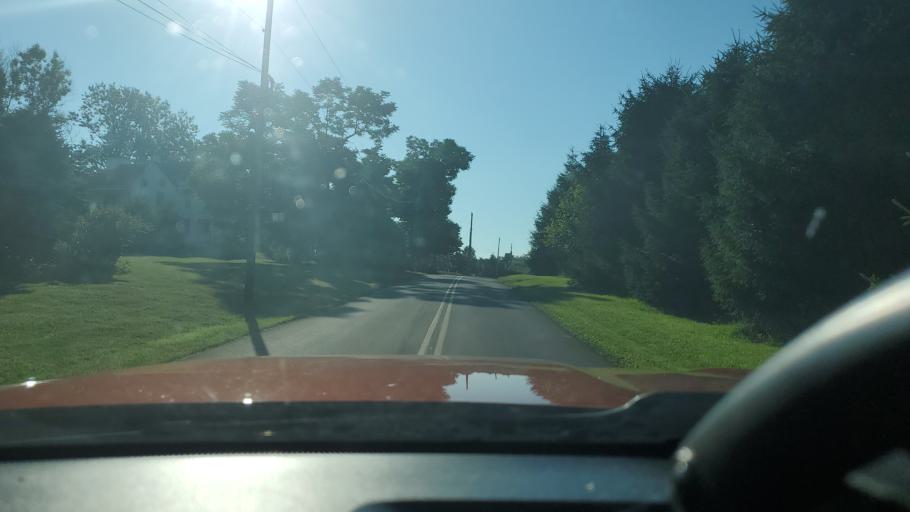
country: US
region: Pennsylvania
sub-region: Montgomery County
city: Harleysville
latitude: 40.2995
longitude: -75.4013
